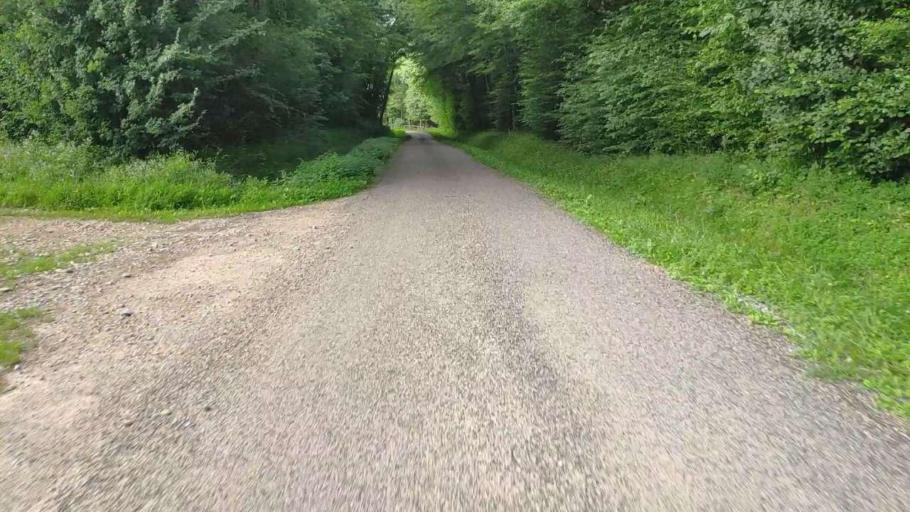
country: FR
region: Franche-Comte
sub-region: Departement du Jura
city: Bletterans
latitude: 46.8355
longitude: 5.5213
